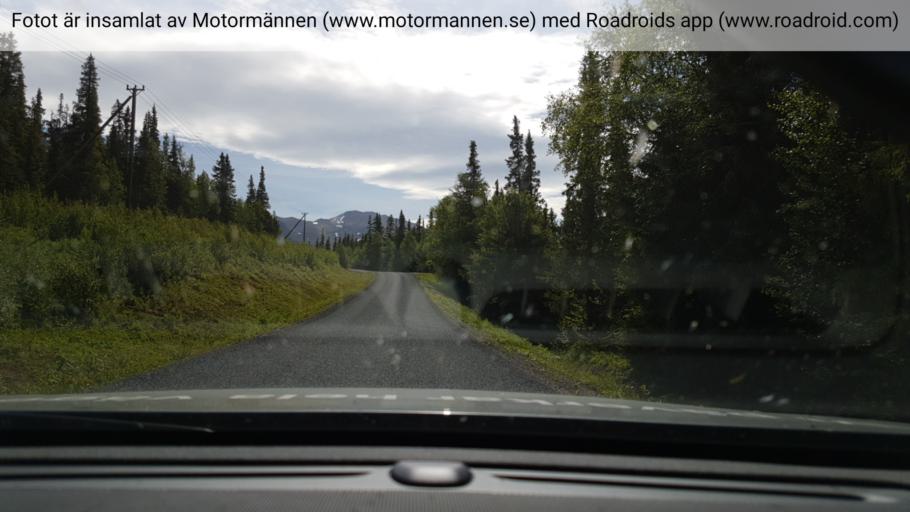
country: SE
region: Vaesterbotten
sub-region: Vilhelmina Kommun
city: Sjoberg
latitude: 65.2705
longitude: 15.3683
